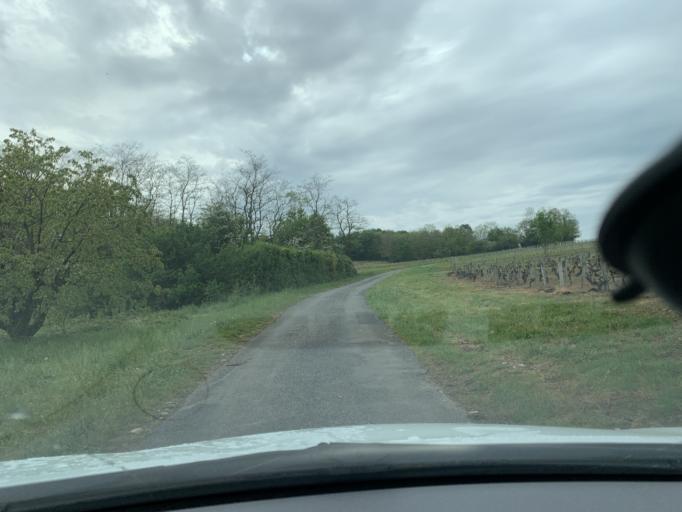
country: FR
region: Rhone-Alpes
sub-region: Departement du Rhone
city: Charnay
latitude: 45.9165
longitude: 4.6627
